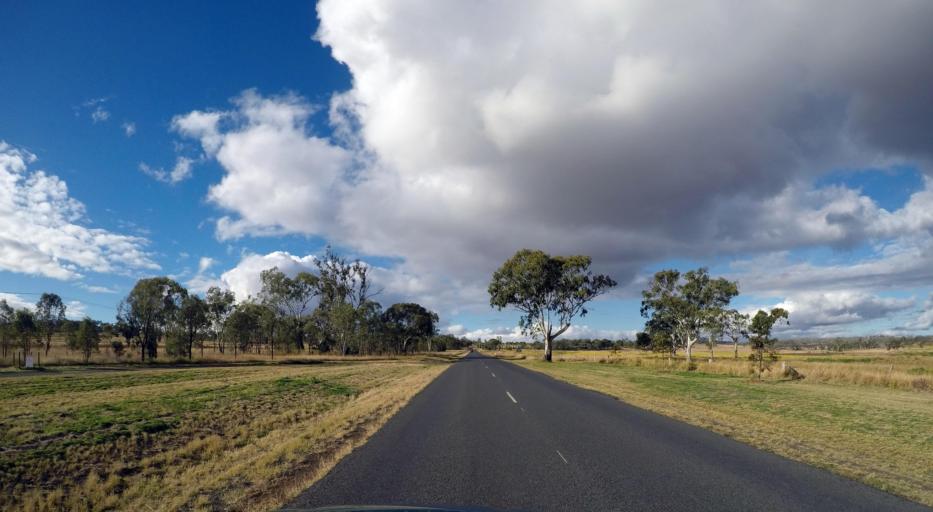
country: AU
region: Queensland
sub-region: Toowoomba
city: Westbrook
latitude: -27.7051
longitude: 151.6538
